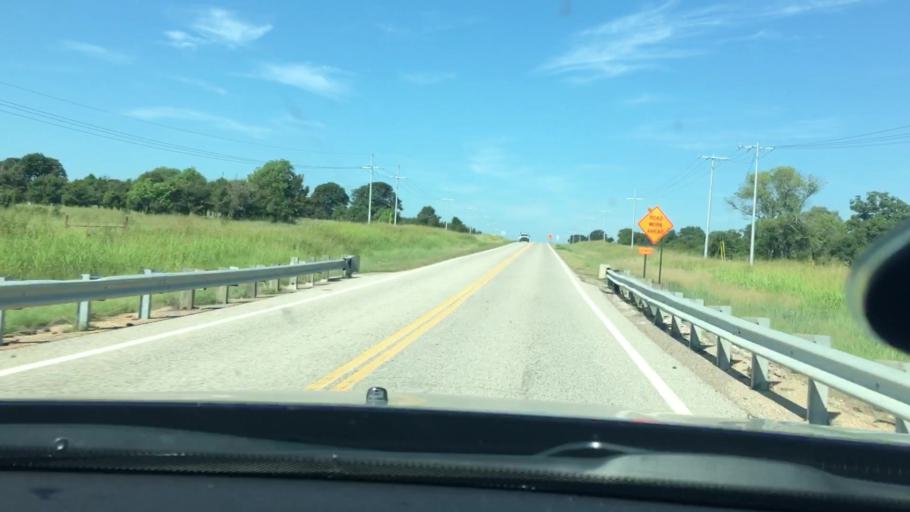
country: US
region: Oklahoma
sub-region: Johnston County
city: Tishomingo
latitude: 34.3613
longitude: -96.6231
